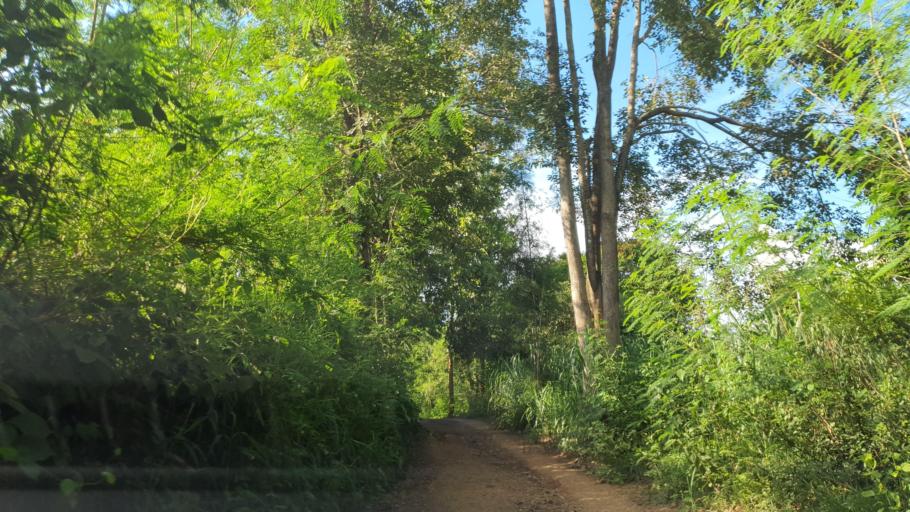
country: TH
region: Chiang Mai
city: Hang Dong
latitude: 18.7199
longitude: 98.8530
